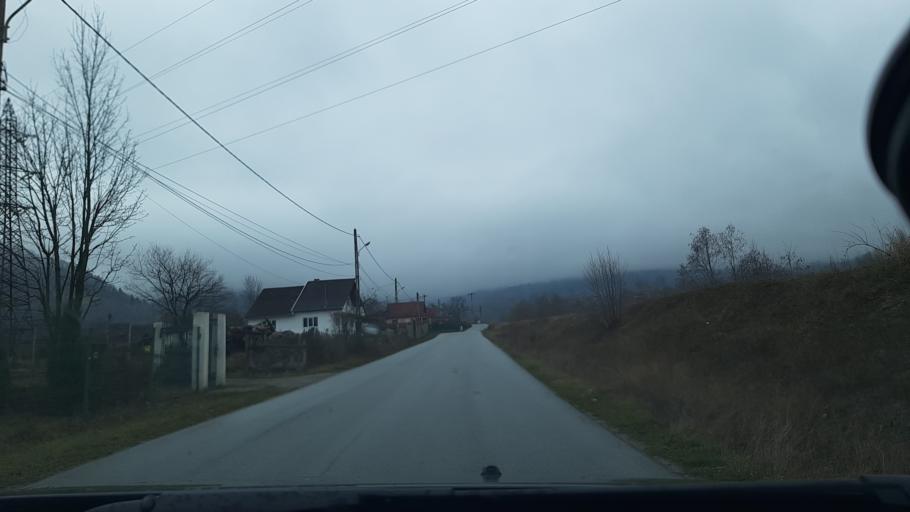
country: RO
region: Hunedoara
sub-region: Oras Petrila
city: Petrila
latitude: 45.4279
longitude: 23.4225
